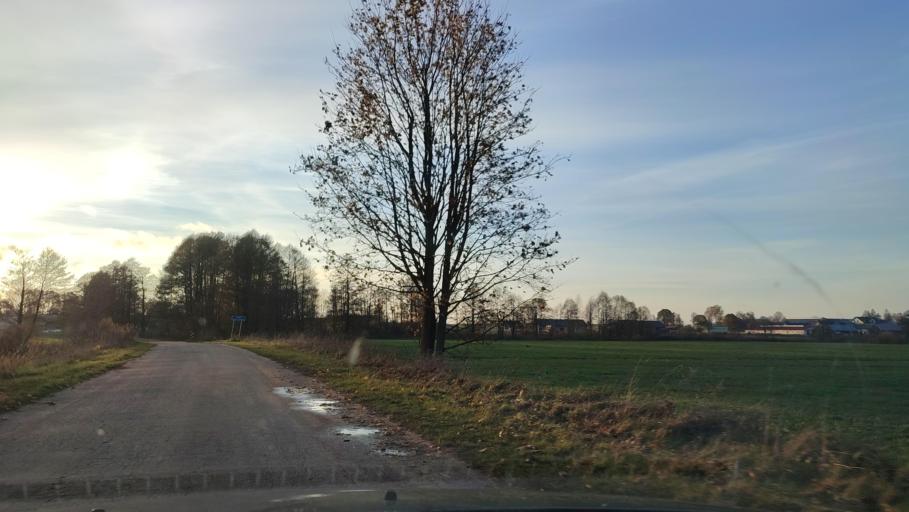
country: PL
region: Masovian Voivodeship
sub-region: Powiat mlawski
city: Dzierzgowo
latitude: 53.2600
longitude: 20.6090
